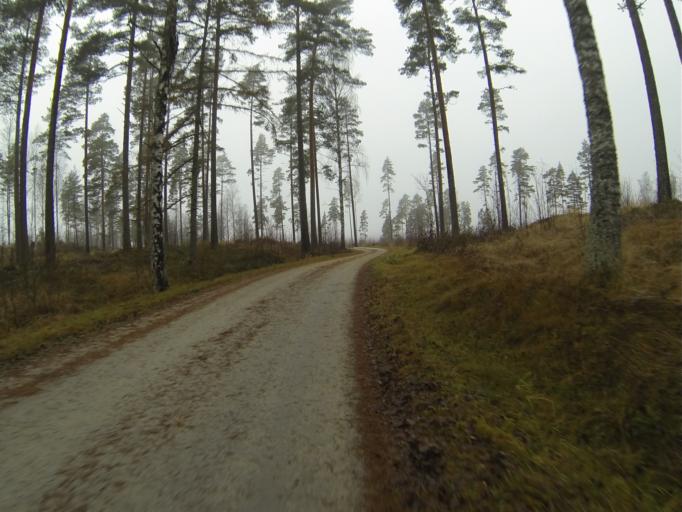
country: FI
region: Varsinais-Suomi
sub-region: Salo
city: Halikko
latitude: 60.4079
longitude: 22.9543
